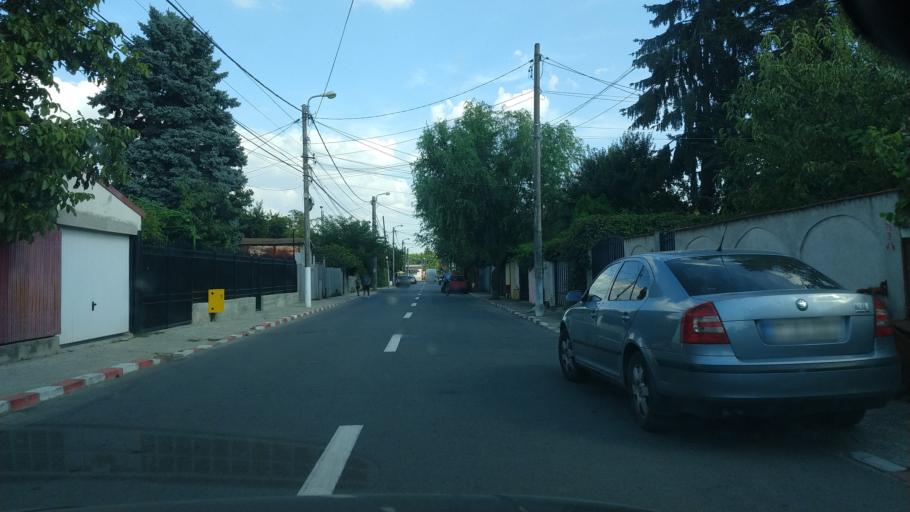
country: RO
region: Ilfov
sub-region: Voluntari City
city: Voluntari
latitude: 44.4904
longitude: 26.1676
